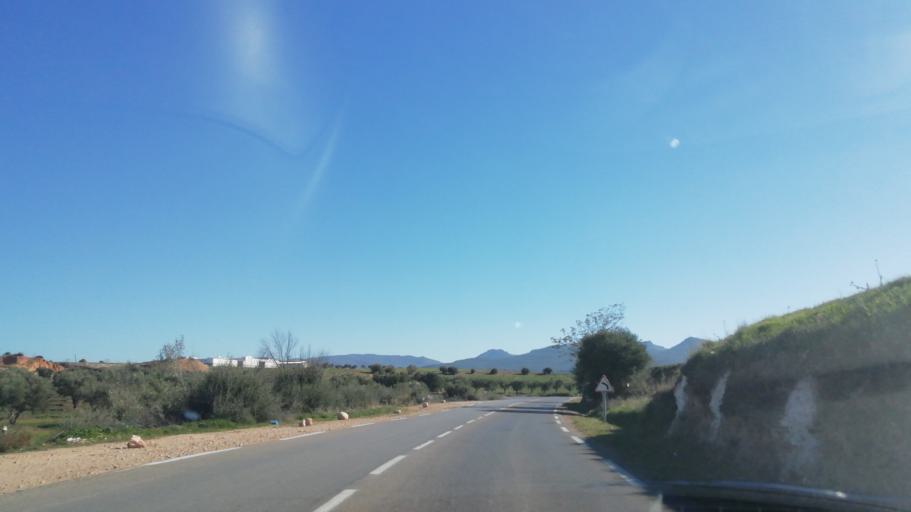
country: DZ
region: Tlemcen
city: Beni Mester
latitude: 34.8249
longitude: -1.5692
